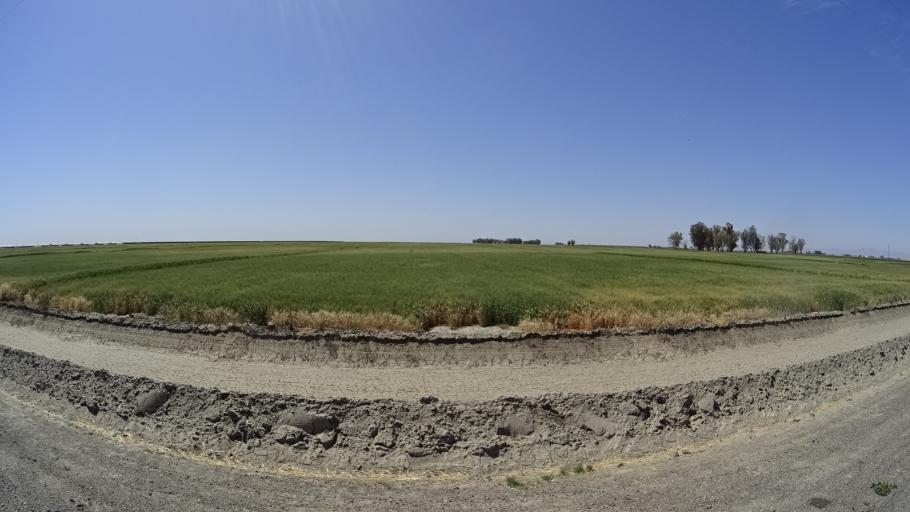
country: US
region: California
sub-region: Kings County
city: Stratford
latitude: 36.1900
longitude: -119.7587
